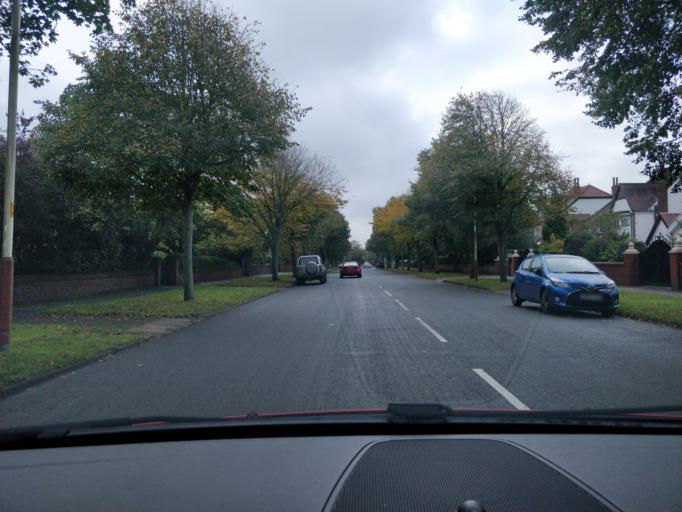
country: GB
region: England
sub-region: Sefton
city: Southport
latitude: 53.6176
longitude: -3.0215
